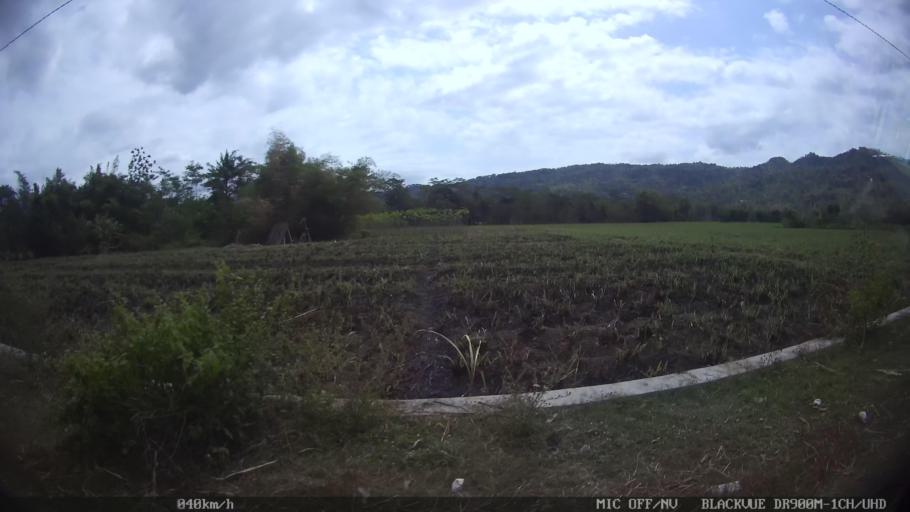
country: ID
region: Central Java
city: Candi Prambanan
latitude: -7.8101
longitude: 110.5056
